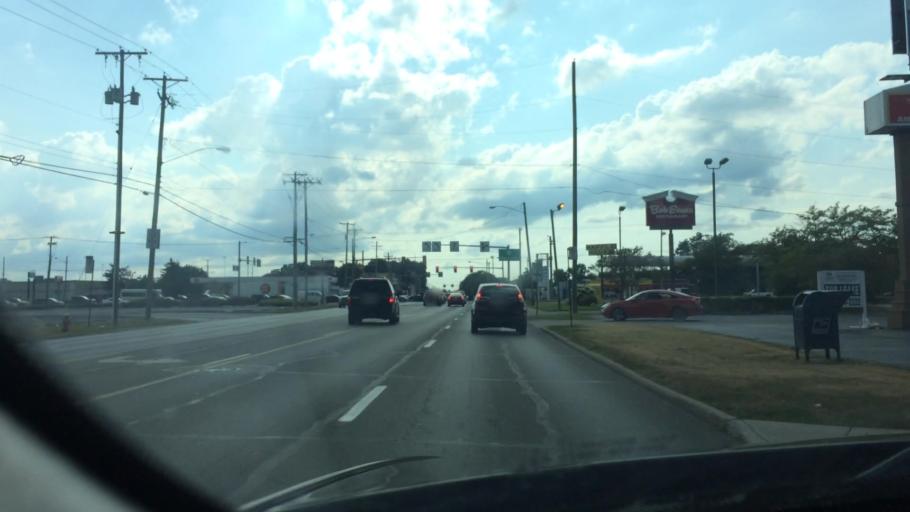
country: US
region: Ohio
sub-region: Lucas County
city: Maumee
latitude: 41.5947
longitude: -83.6628
